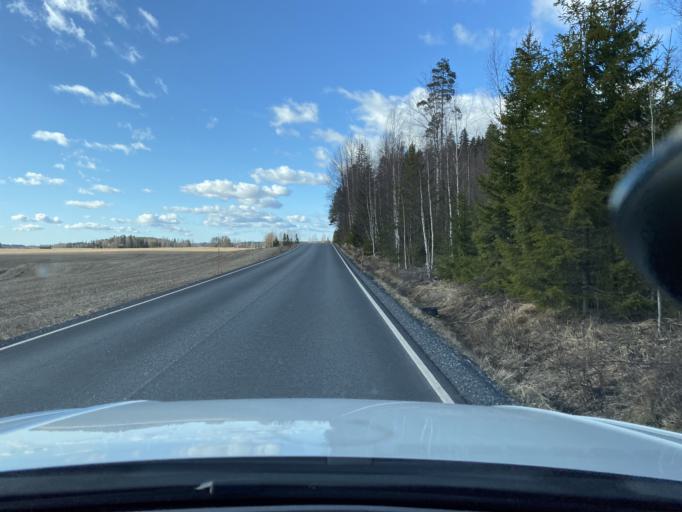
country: FI
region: Pirkanmaa
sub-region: Lounais-Pirkanmaa
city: Punkalaidun
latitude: 61.0777
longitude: 23.2155
